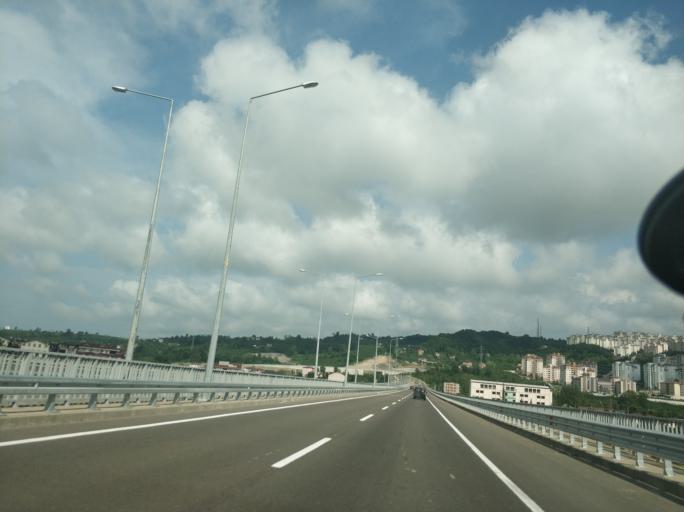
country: TR
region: Ordu
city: Ordu
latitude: 40.9555
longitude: 37.8928
